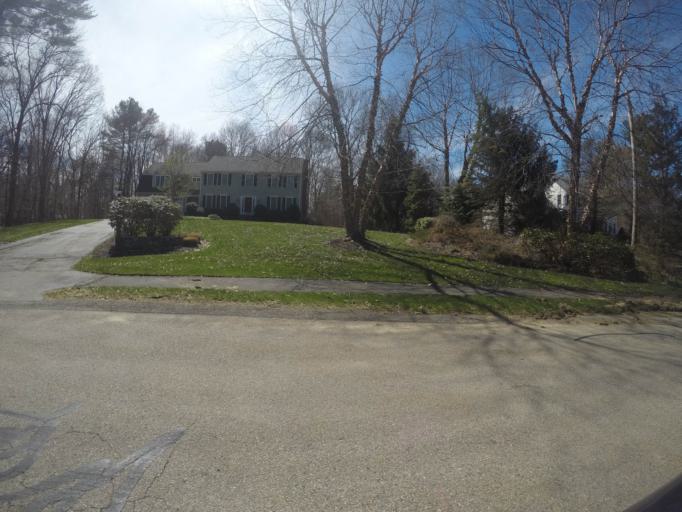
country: US
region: Massachusetts
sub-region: Bristol County
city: Easton
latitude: 42.0281
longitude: -71.0822
